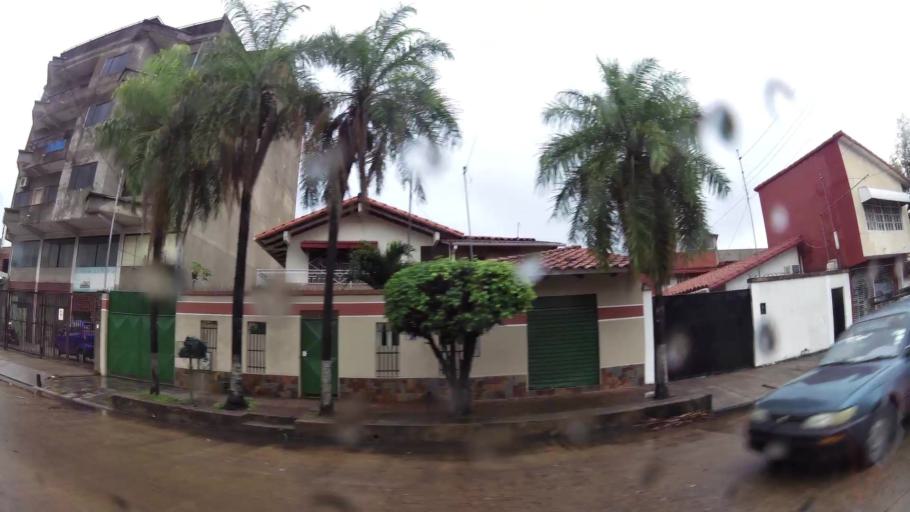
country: BO
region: Santa Cruz
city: Santa Cruz de la Sierra
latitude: -17.8108
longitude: -63.2037
